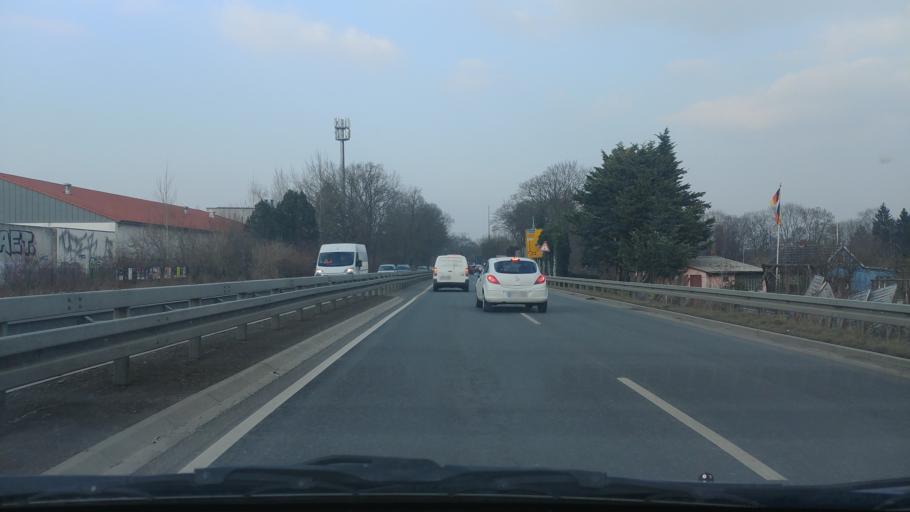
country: DE
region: Lower Saxony
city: Hemmingen
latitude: 52.3360
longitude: 9.7193
